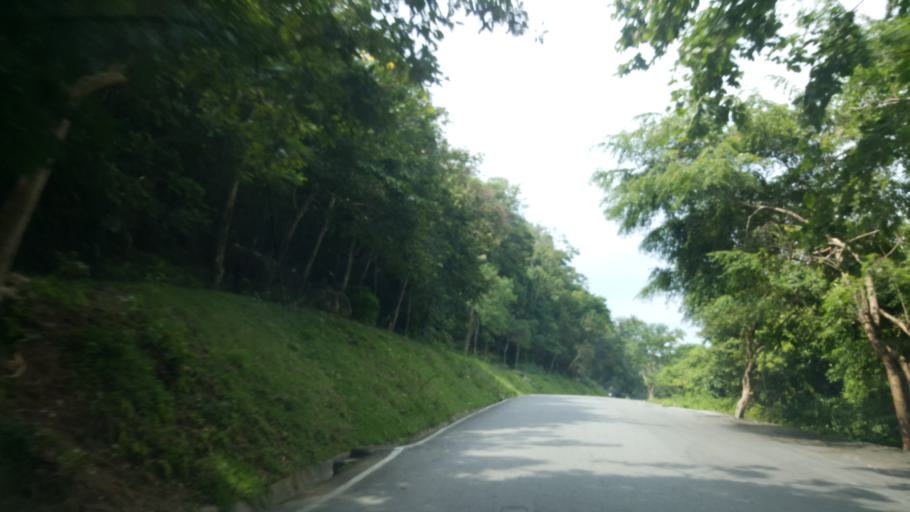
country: TH
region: Chon Buri
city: Ban Bueng
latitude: 13.2107
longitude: 101.0629
